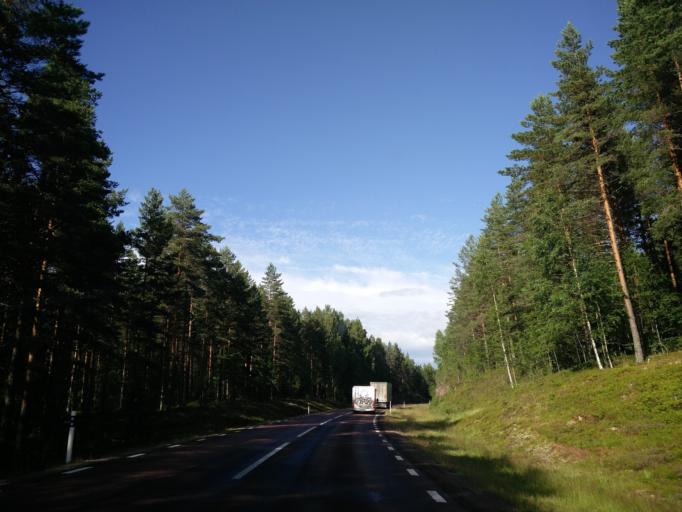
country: SE
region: Vaermland
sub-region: Hagfors Kommun
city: Ekshaerad
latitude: 60.4788
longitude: 13.3090
